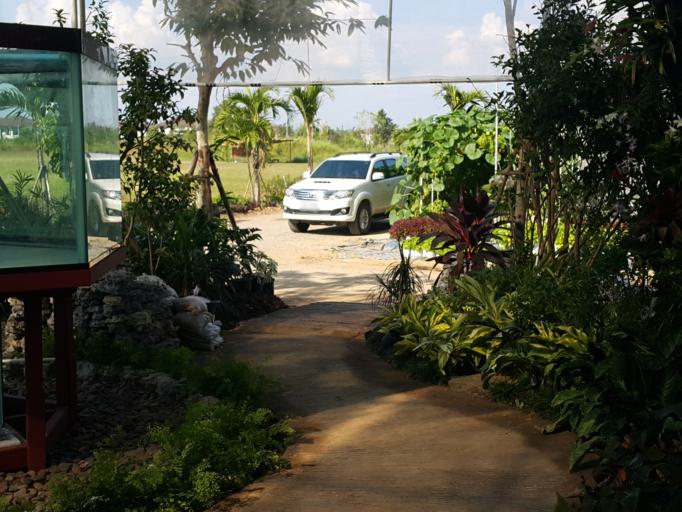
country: TH
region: Chiang Mai
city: San Kamphaeng
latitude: 18.7362
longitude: 99.0900
